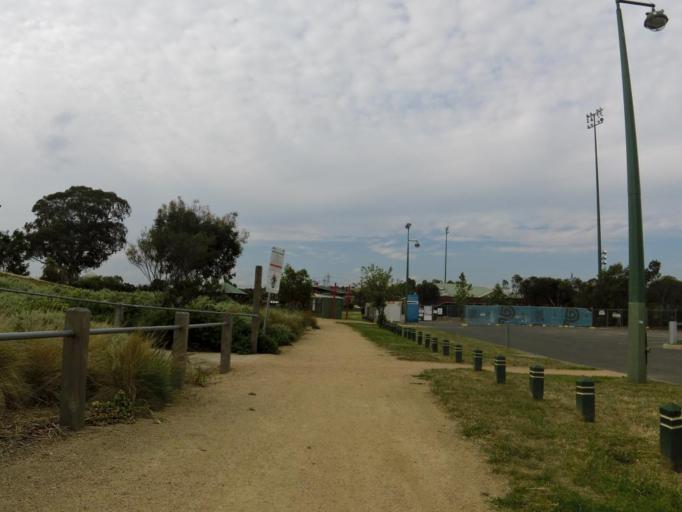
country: AU
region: Victoria
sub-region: Whittlesea
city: Mill Park
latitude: -37.6470
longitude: 145.0569
